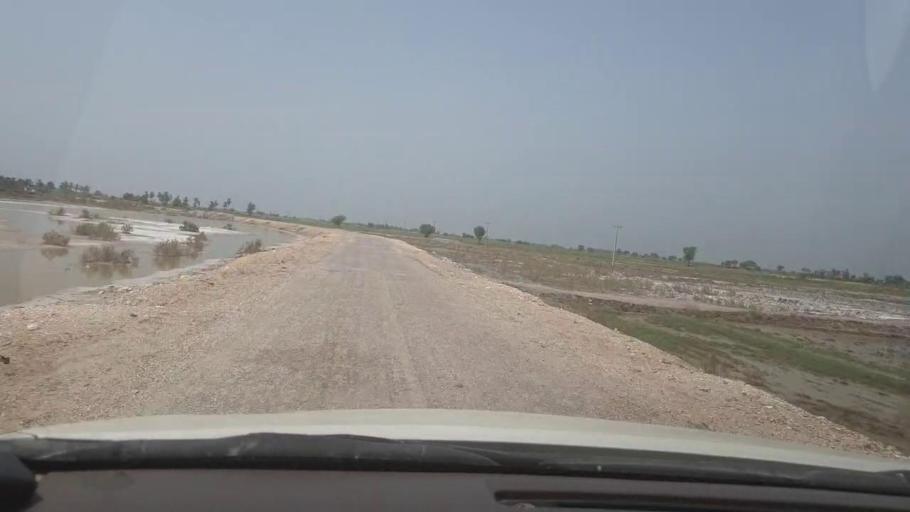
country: PK
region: Sindh
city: Garhi Yasin
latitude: 27.9755
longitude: 68.5477
